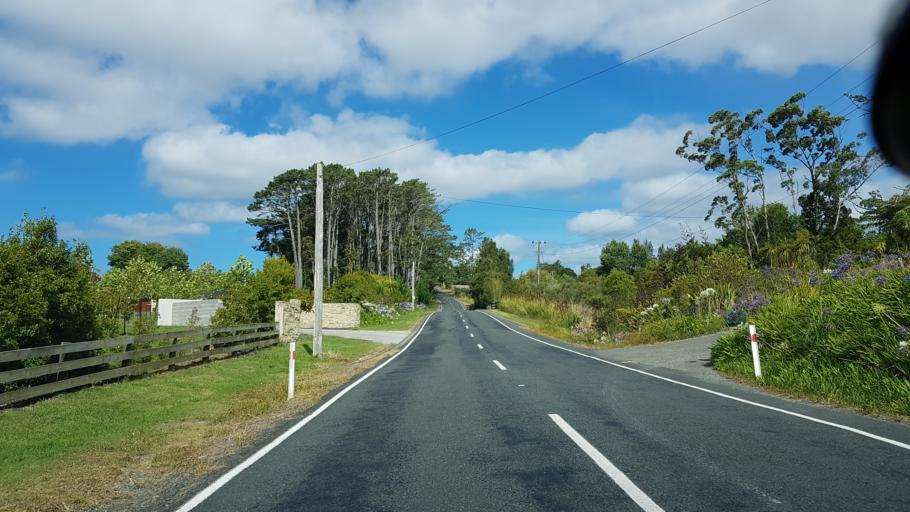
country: NZ
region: Auckland
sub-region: Auckland
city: Rothesay Bay
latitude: -36.6902
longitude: 174.6742
